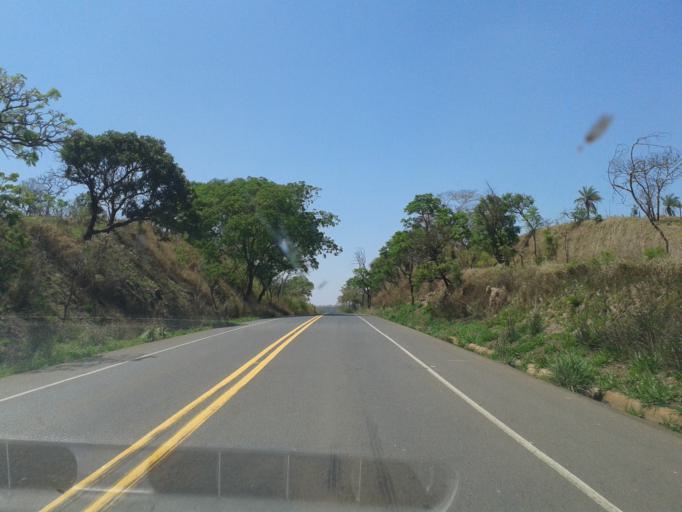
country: BR
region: Minas Gerais
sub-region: Araxa
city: Araxa
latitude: -19.4718
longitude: -47.1617
